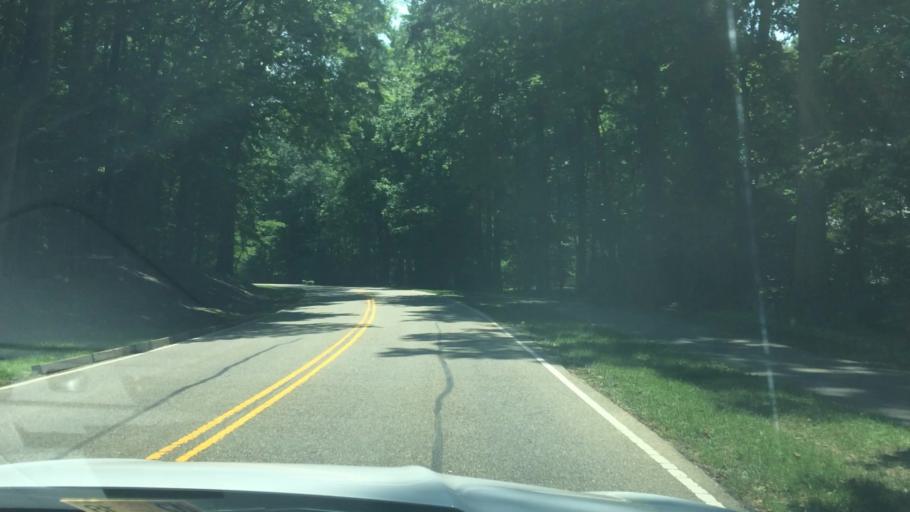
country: US
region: Virginia
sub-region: City of Williamsburg
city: Williamsburg
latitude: 37.2433
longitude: -76.6665
